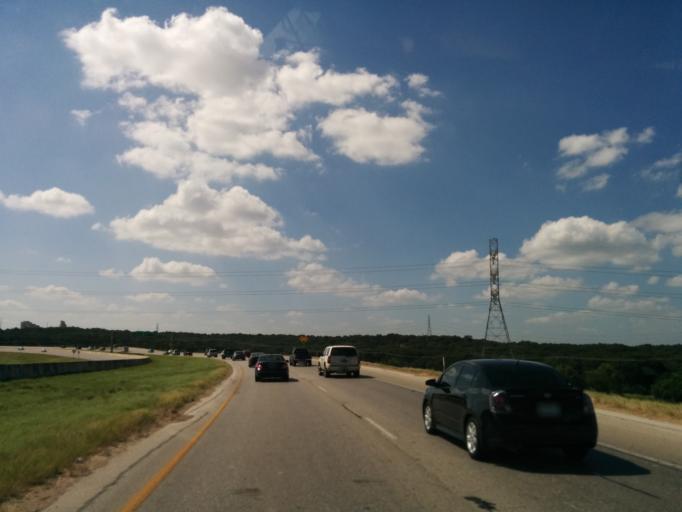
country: US
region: Texas
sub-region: Bexar County
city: Live Oak
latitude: 29.6005
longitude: -98.3578
